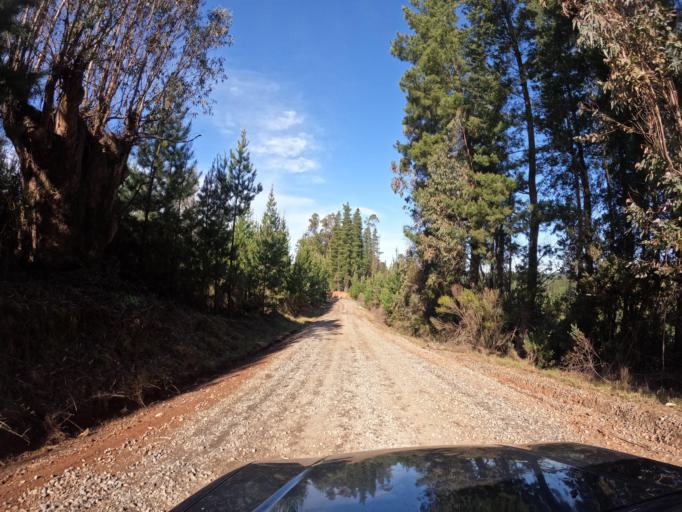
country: CL
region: Biobio
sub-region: Provincia de Biobio
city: La Laja
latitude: -37.0837
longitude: -72.7821
